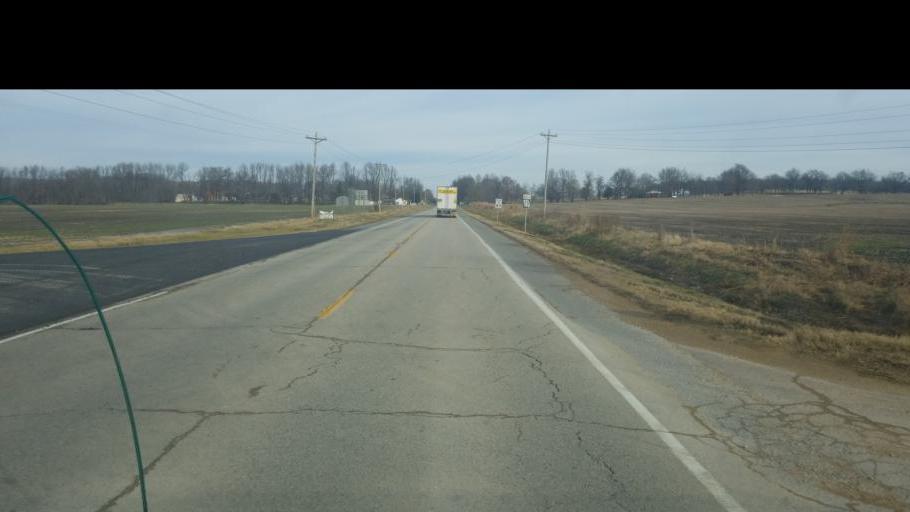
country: US
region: Missouri
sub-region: Stoddard County
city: Bloomfield
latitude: 36.9003
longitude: -89.9227
